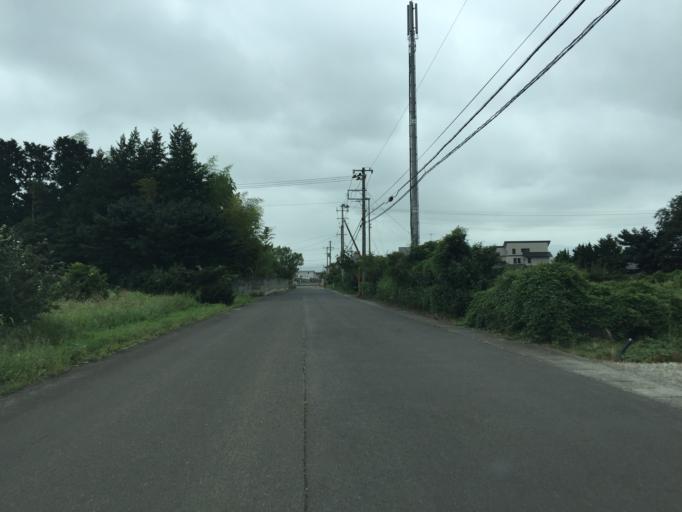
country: JP
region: Fukushima
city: Fukushima-shi
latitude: 37.7745
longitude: 140.3837
